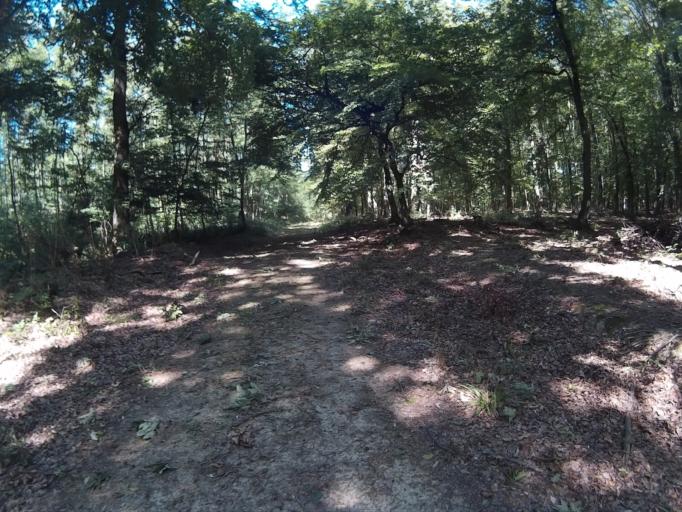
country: HU
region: Zala
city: Zalalovo
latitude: 46.8103
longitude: 16.6419
